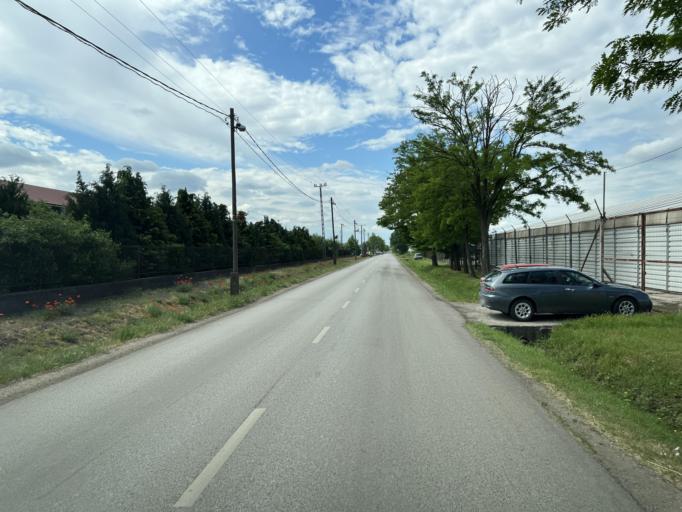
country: HU
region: Pest
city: Szentlorinckata
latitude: 47.5144
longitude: 19.7464
